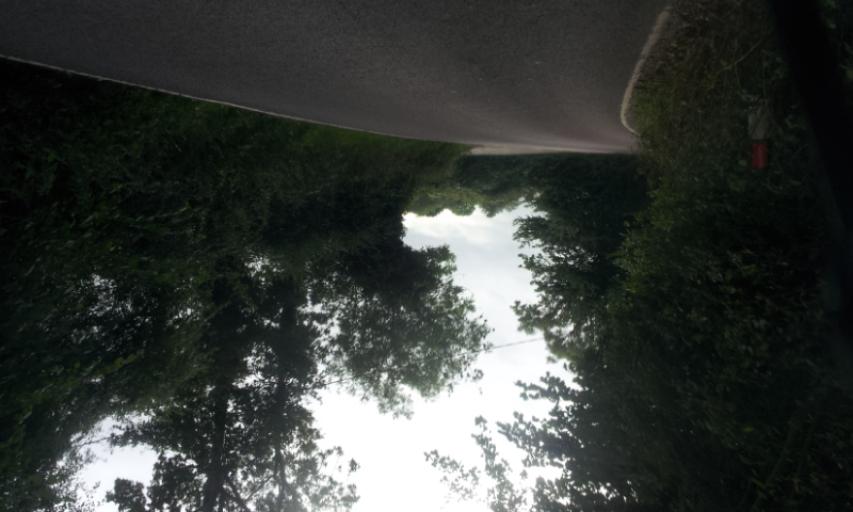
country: GB
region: England
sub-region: Kent
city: Hadlow
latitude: 51.2179
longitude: 0.3030
